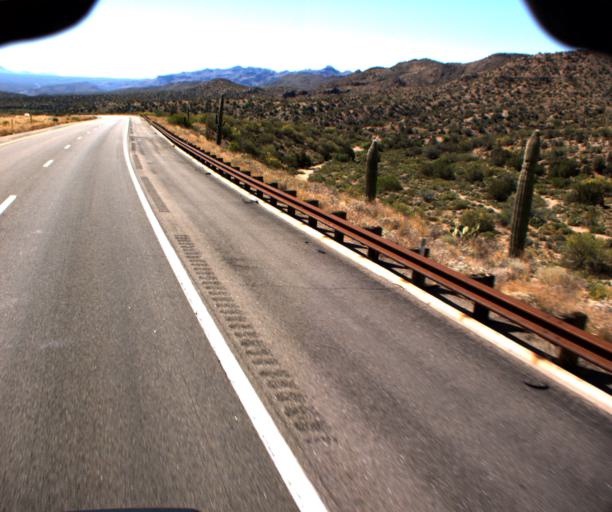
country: US
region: Arizona
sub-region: Yavapai County
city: Bagdad
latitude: 34.4345
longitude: -113.2556
